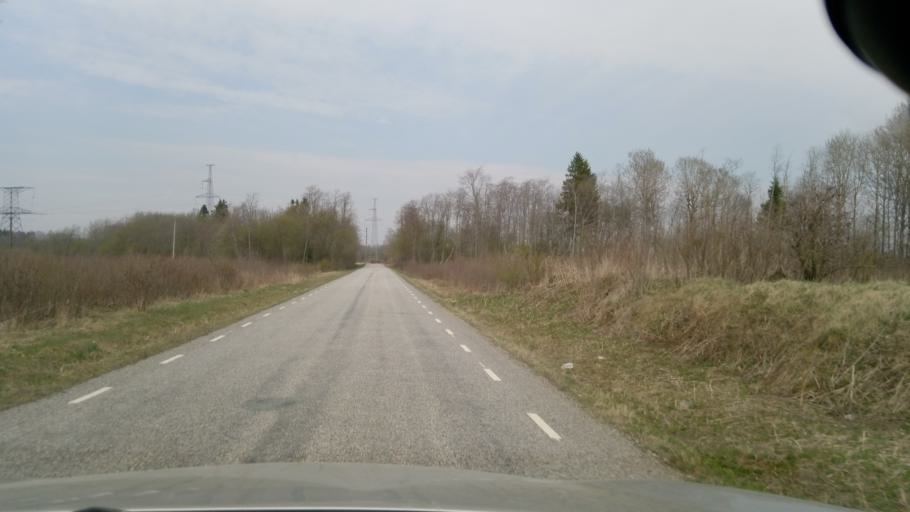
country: EE
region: Jaervamaa
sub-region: Tueri vald
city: Tueri
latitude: 58.7939
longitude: 25.4791
